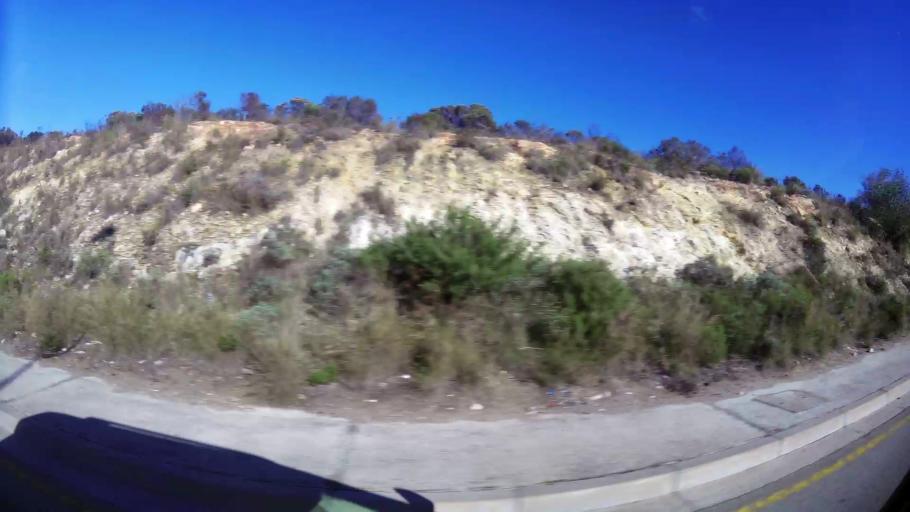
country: ZA
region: Eastern Cape
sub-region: Nelson Mandela Bay Metropolitan Municipality
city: Port Elizabeth
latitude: -33.9797
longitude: 25.6349
